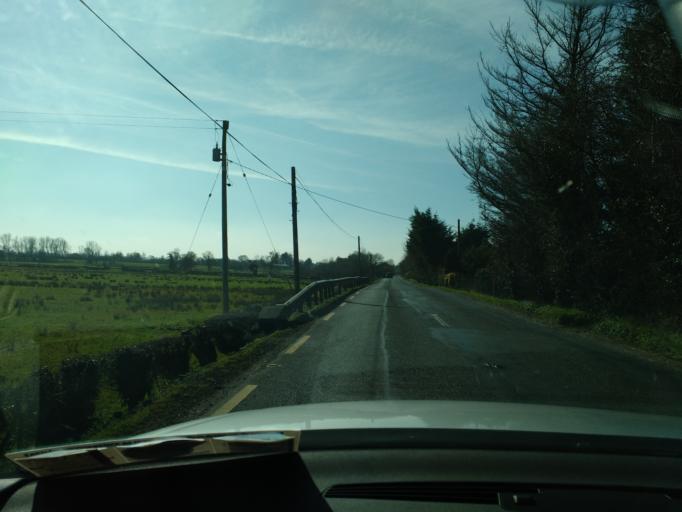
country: IE
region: Munster
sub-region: North Tipperary
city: Newport
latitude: 52.7037
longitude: -8.4547
